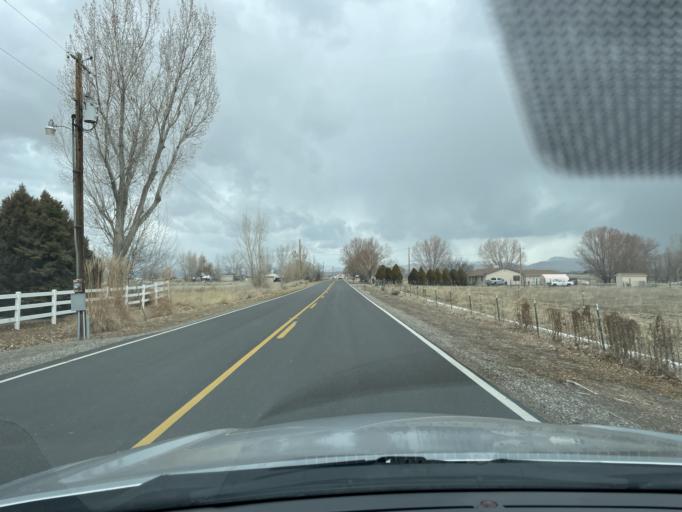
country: US
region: Colorado
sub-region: Mesa County
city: Loma
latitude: 39.2051
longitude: -108.8082
